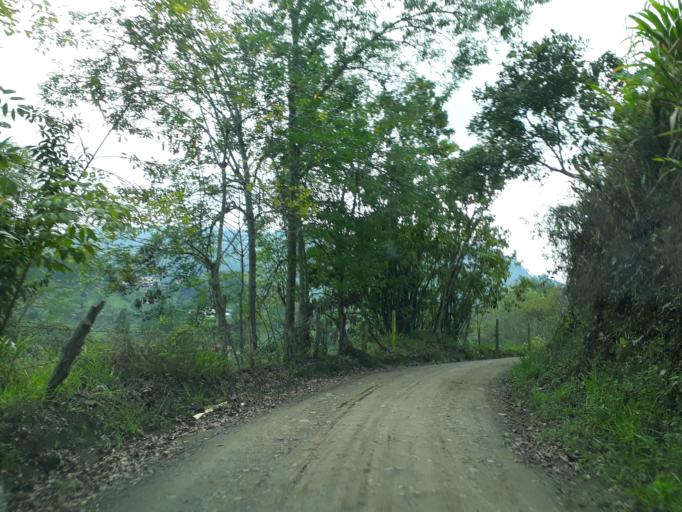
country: CO
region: Cundinamarca
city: Manta
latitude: 5.0039
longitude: -73.5367
